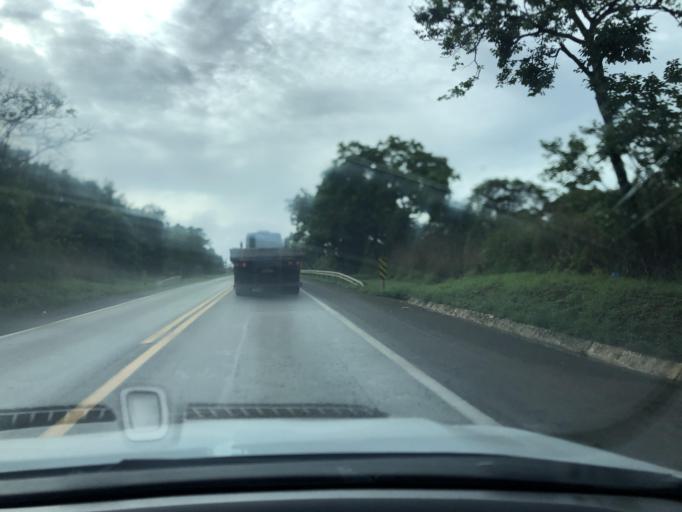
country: BR
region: Goias
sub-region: Cristalina
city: Cristalina
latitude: -16.6607
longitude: -47.7240
